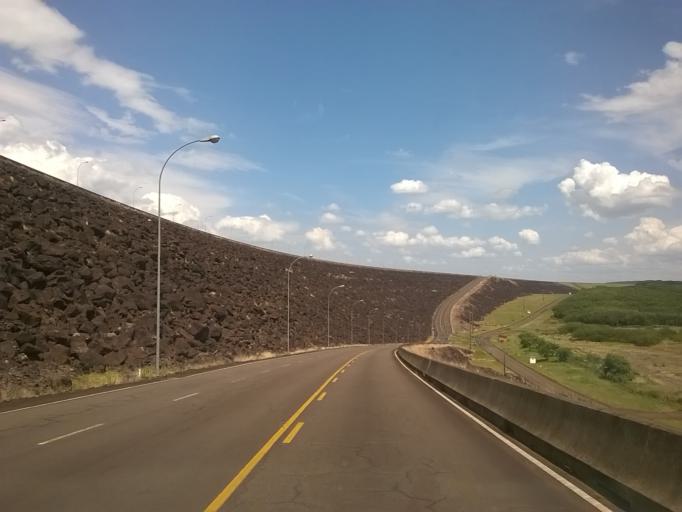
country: PY
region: Alto Parana
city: Ciudad del Este
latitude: -25.4102
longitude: -54.5780
